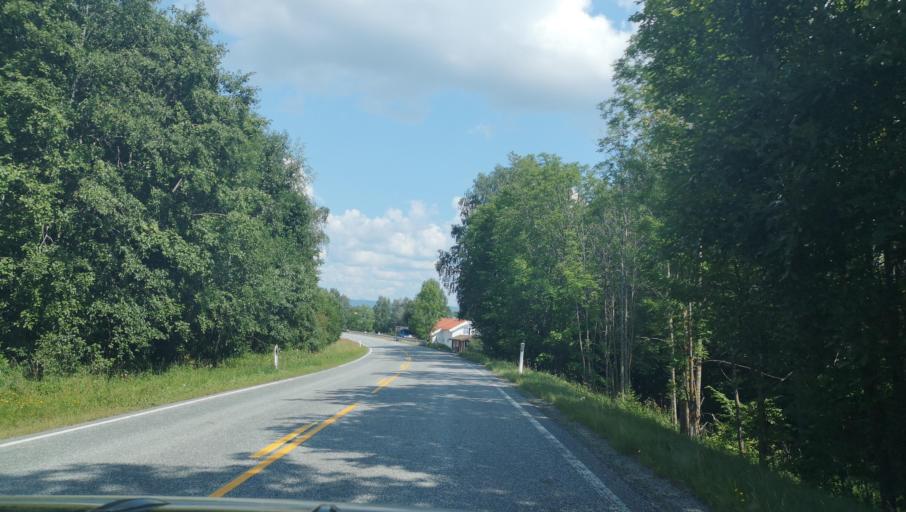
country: NO
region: Buskerud
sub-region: Ovre Eiker
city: Hokksund
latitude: 59.7089
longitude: 9.8158
